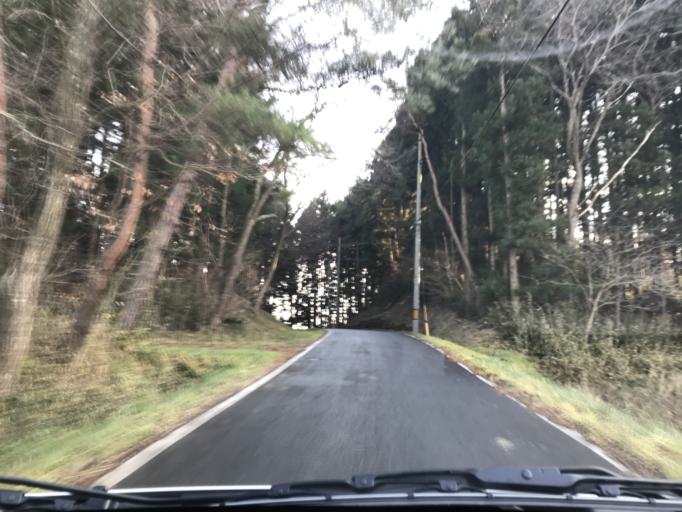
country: JP
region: Miyagi
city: Wakuya
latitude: 38.6855
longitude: 141.1121
